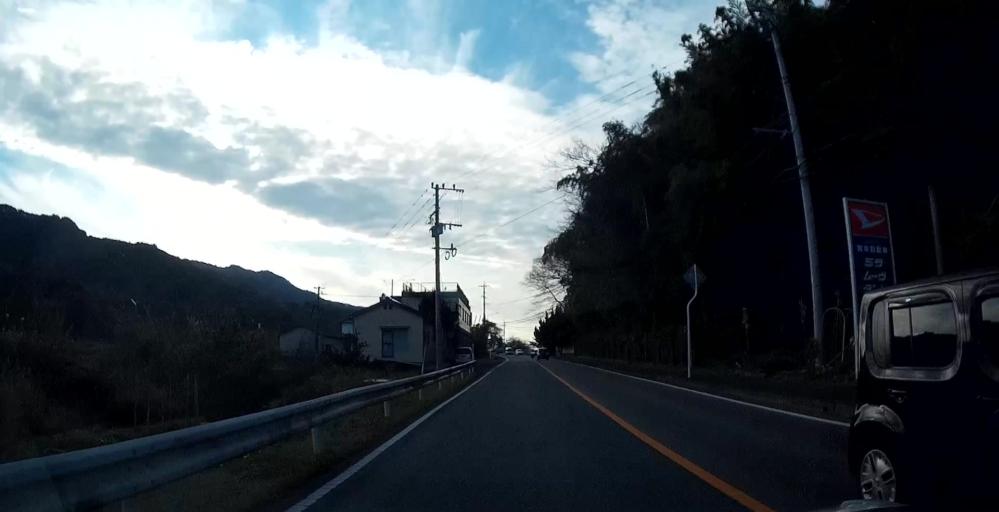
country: JP
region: Kumamoto
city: Uto
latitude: 32.6685
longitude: 130.5489
